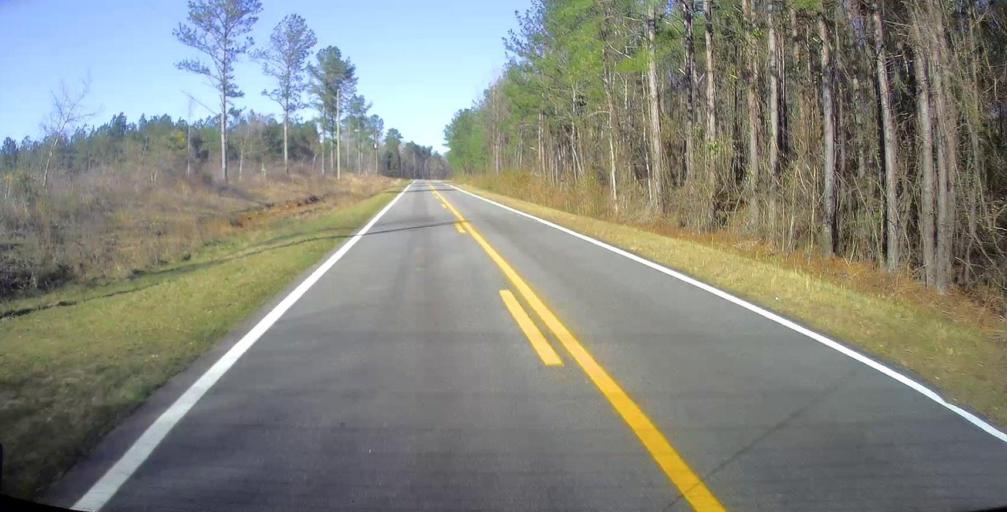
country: US
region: Georgia
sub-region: Taylor County
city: Reynolds
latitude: 32.5723
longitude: -83.9982
